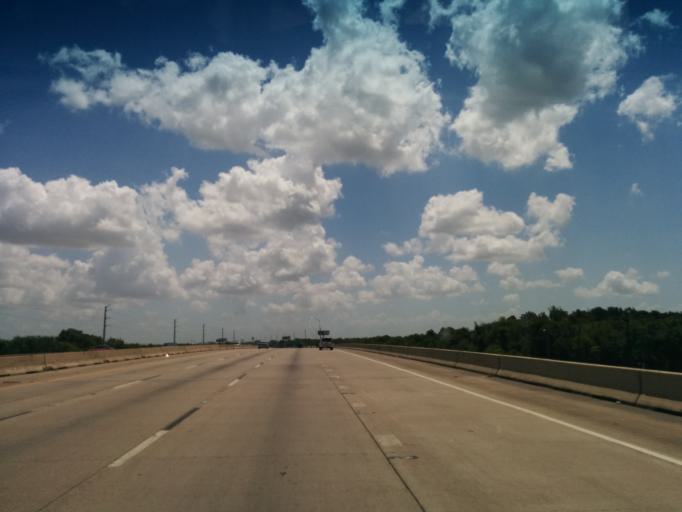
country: US
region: Texas
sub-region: Harris County
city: Highlands
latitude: 29.7998
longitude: -95.0179
